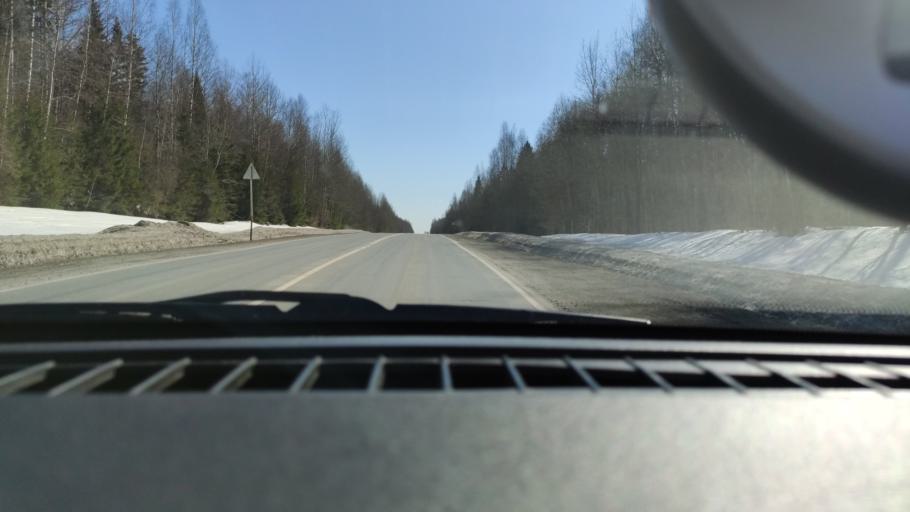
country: RU
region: Perm
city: Perm
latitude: 58.1536
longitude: 56.2536
